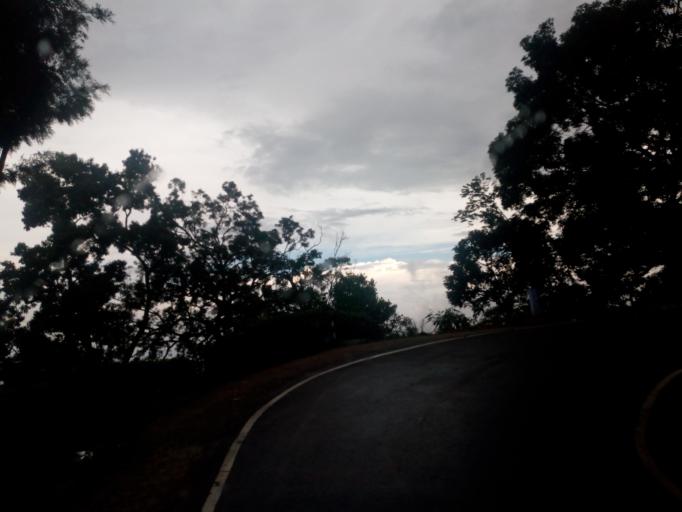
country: IN
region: Tamil Nadu
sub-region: Nilgiri
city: Kotagiri
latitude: 11.3615
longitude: 76.8484
